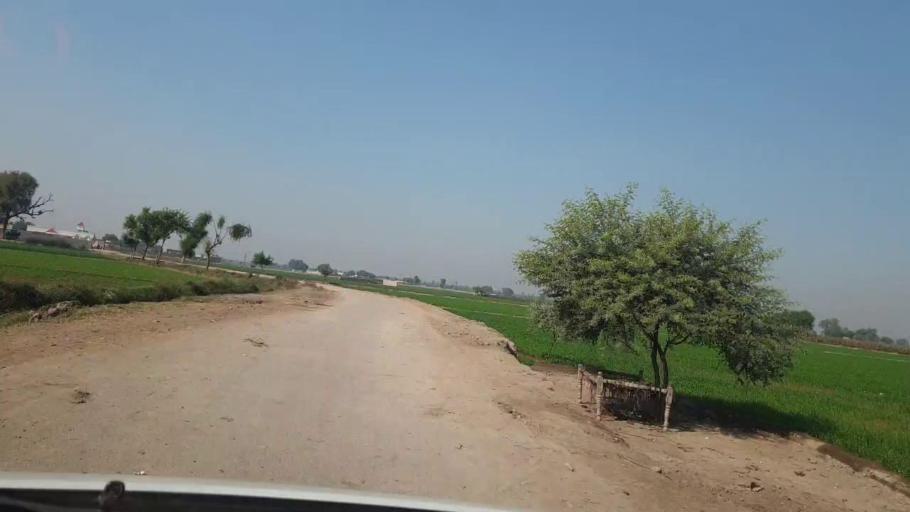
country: PK
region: Sindh
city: Bhan
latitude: 26.6449
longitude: 67.7051
